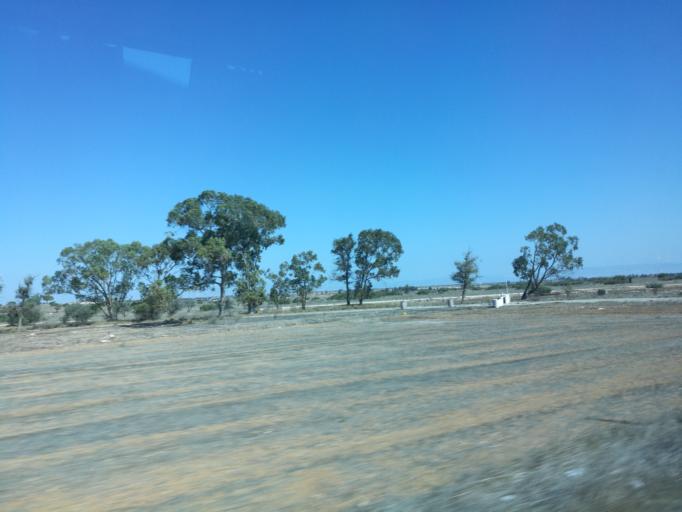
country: CY
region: Ammochostos
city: Achna
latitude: 35.0585
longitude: 33.7966
